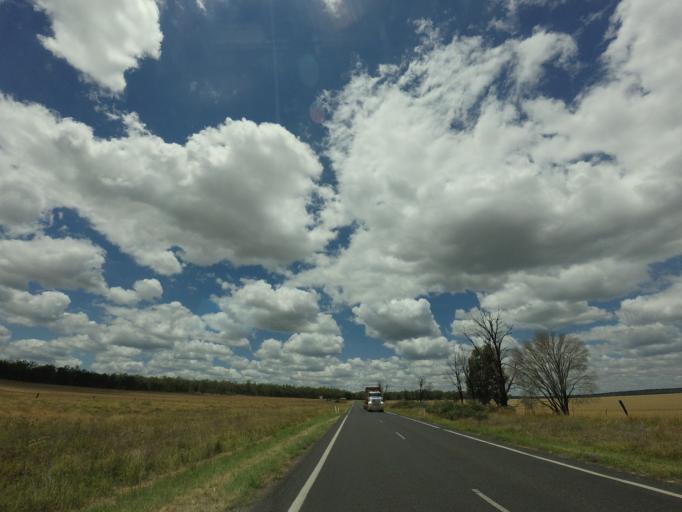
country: AU
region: Queensland
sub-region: Goondiwindi
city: Goondiwindi
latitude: -28.0030
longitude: 150.8939
